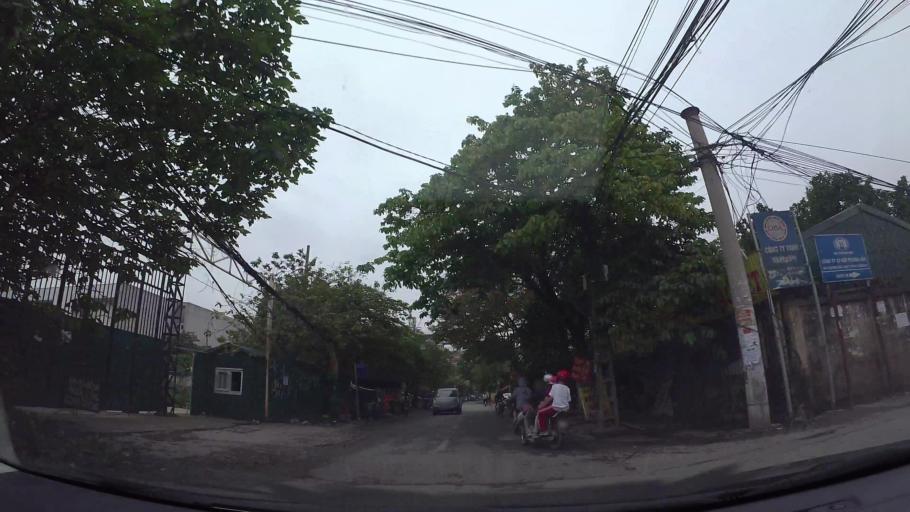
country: VN
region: Ha Noi
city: Hai BaTrung
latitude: 20.9967
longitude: 105.8798
